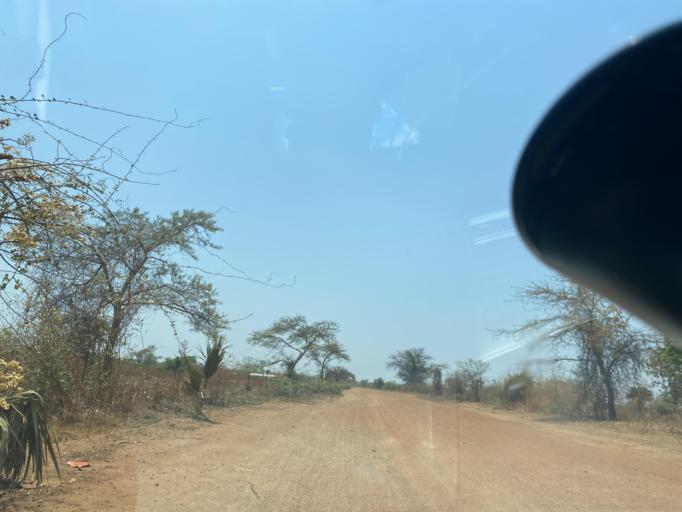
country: ZM
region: Lusaka
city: Lusaka
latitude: -15.4612
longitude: 27.9225
